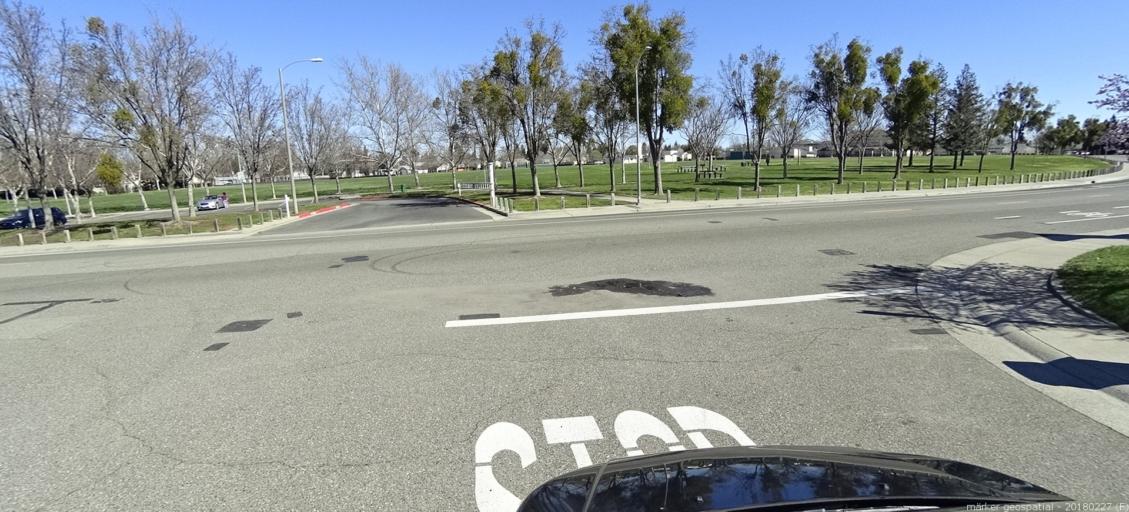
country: US
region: California
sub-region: Sacramento County
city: Antelope
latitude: 38.7173
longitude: -121.3446
